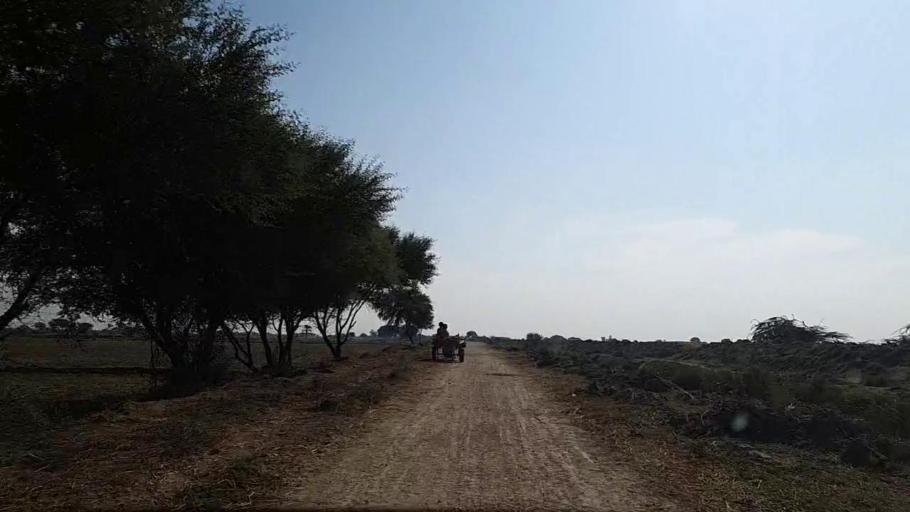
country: PK
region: Sindh
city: Daro Mehar
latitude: 24.7285
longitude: 68.1159
